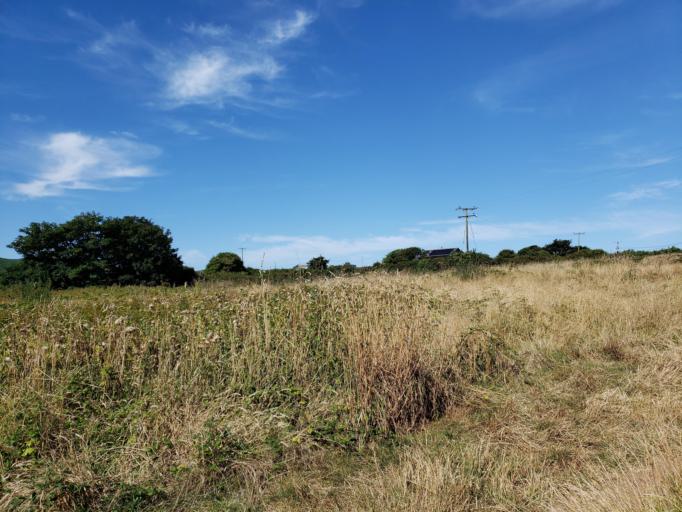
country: GB
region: England
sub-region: Cornwall
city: St Ives
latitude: 50.2074
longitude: -5.4982
